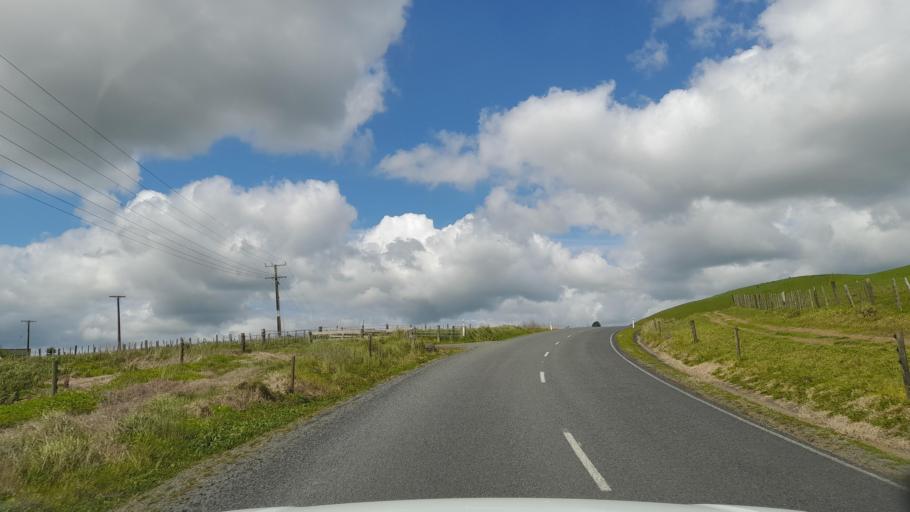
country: NZ
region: Northland
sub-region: Whangarei
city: Maungatapere
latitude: -35.6291
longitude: 174.0815
